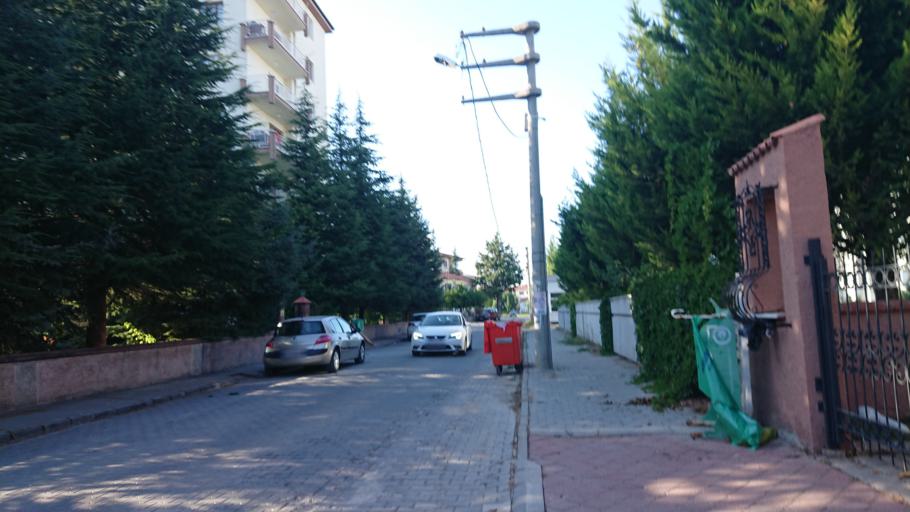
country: TR
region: Eskisehir
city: Eskisehir
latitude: 39.7660
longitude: 30.4931
